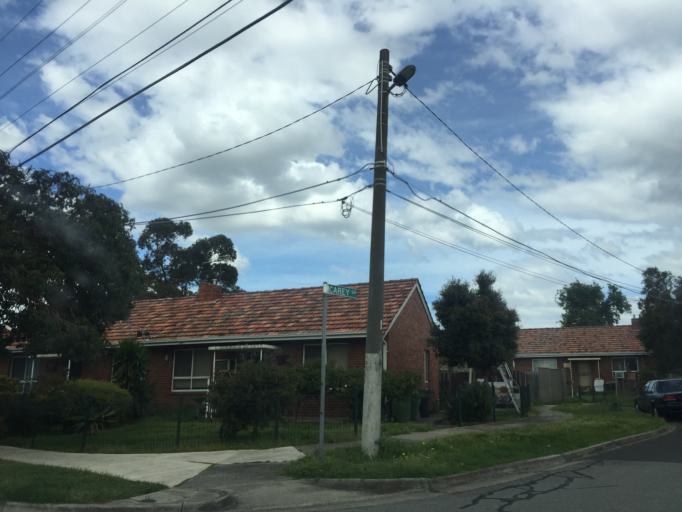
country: AU
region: Victoria
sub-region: Darebin
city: Preston
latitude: -37.7504
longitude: 145.0155
